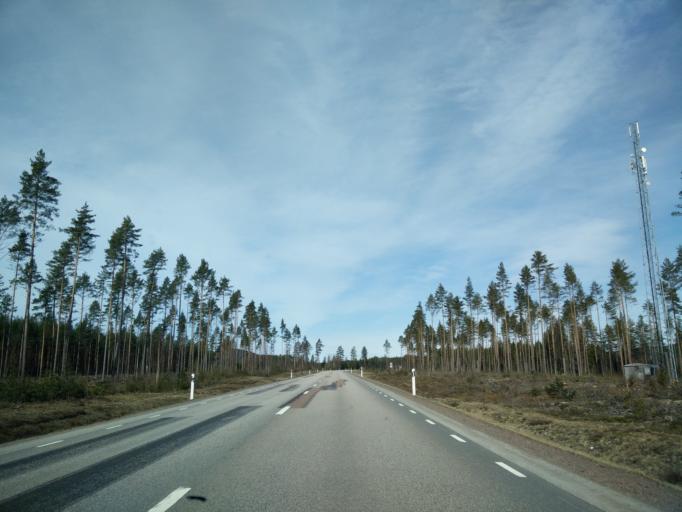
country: SE
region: Vaermland
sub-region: Hagfors Kommun
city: Hagfors
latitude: 60.0176
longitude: 13.5934
